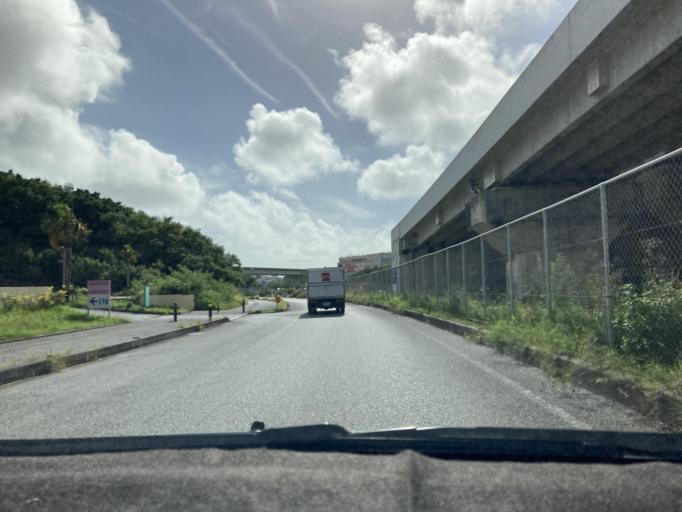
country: JP
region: Okinawa
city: Naha-shi
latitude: 26.2029
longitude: 127.7360
